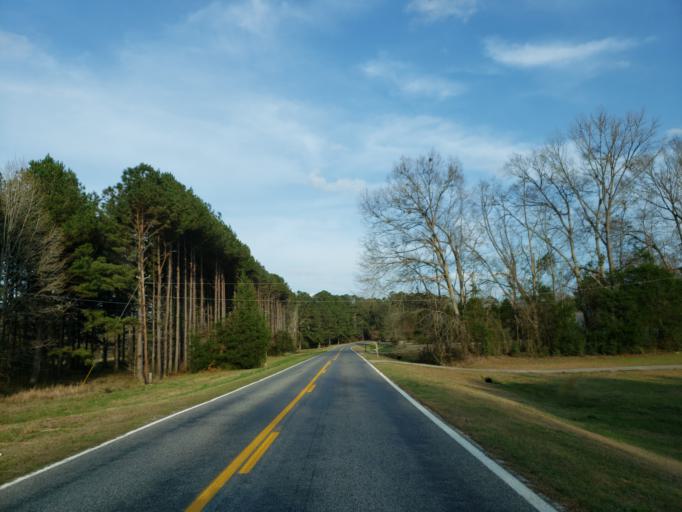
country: US
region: Mississippi
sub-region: Clarke County
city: Stonewall
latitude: 32.1776
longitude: -88.8019
